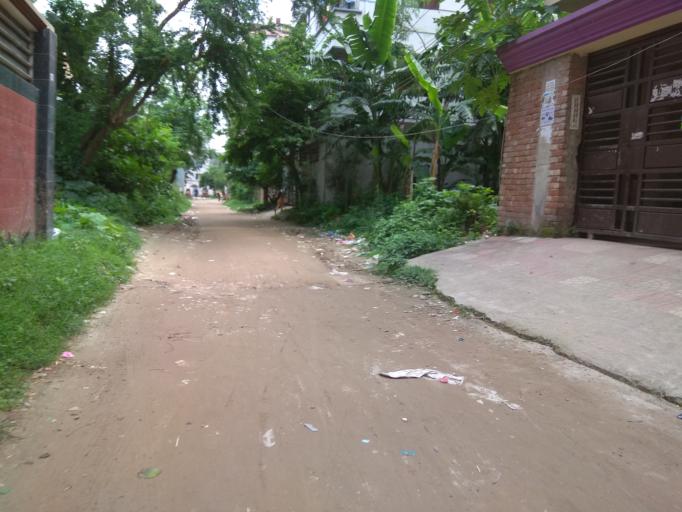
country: BD
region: Dhaka
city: Tungi
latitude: 23.8254
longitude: 90.3518
